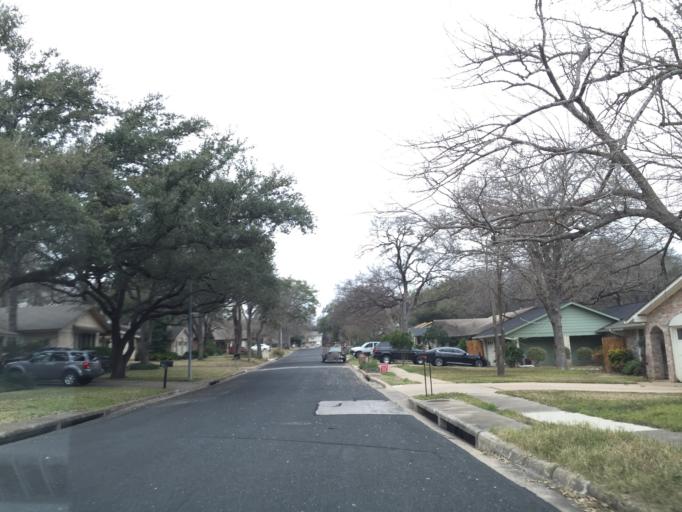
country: US
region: Texas
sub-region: Williamson County
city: Jollyville
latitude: 30.4150
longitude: -97.7386
